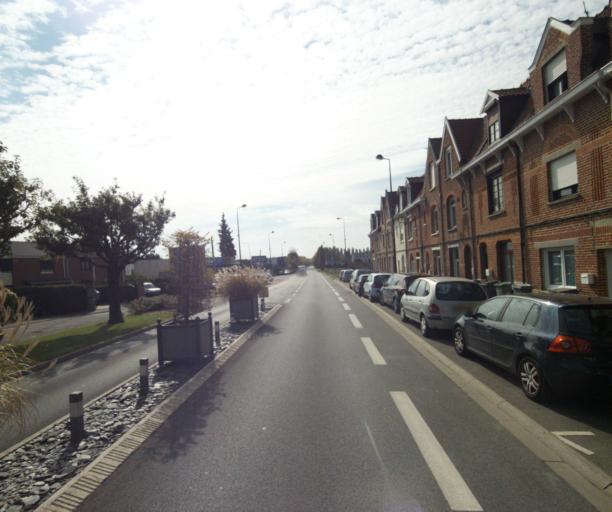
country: FR
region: Nord-Pas-de-Calais
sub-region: Departement du Nord
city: Templemars
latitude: 50.5729
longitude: 3.0468
